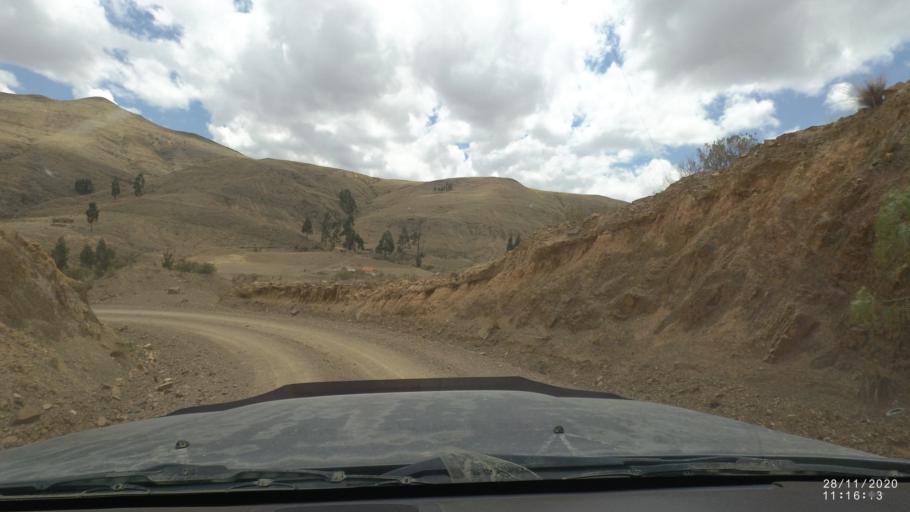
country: BO
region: Cochabamba
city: Tarata
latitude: -17.7472
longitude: -66.0844
